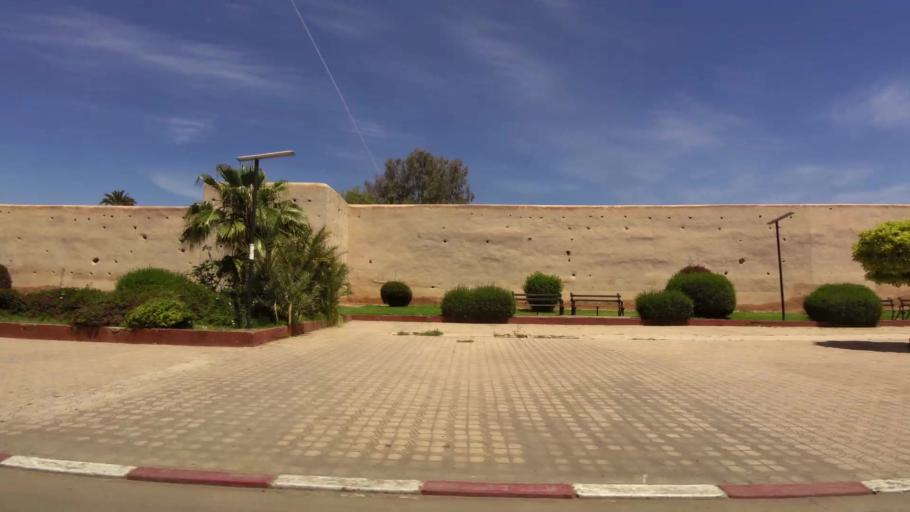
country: MA
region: Marrakech-Tensift-Al Haouz
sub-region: Marrakech
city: Marrakesh
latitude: 31.6303
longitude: -8.0003
